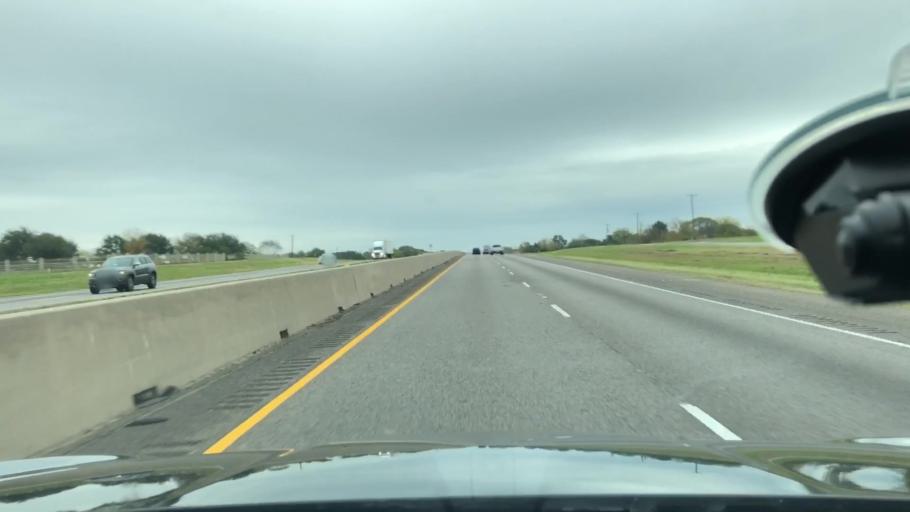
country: US
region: Texas
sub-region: Hopkins County
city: Sulphur Springs
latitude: 33.1467
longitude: -95.5118
